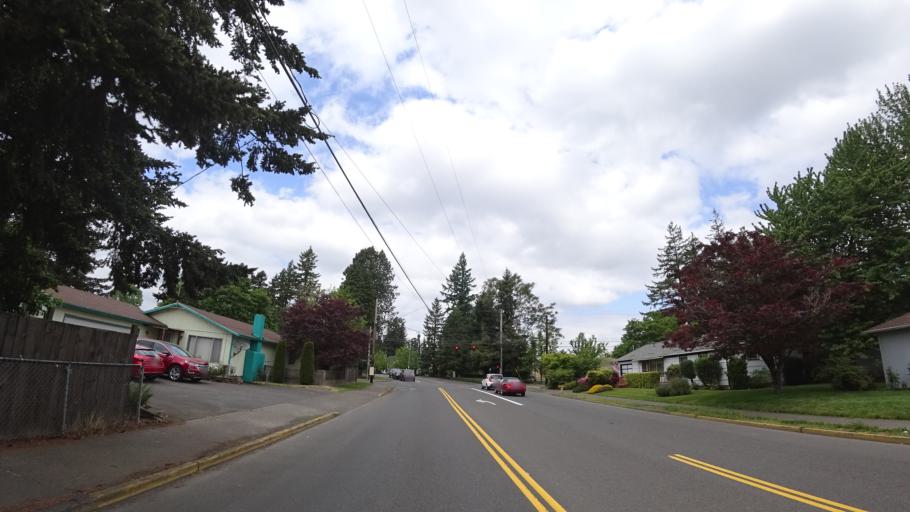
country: US
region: Oregon
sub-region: Multnomah County
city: Lents
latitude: 45.5111
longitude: -122.5482
